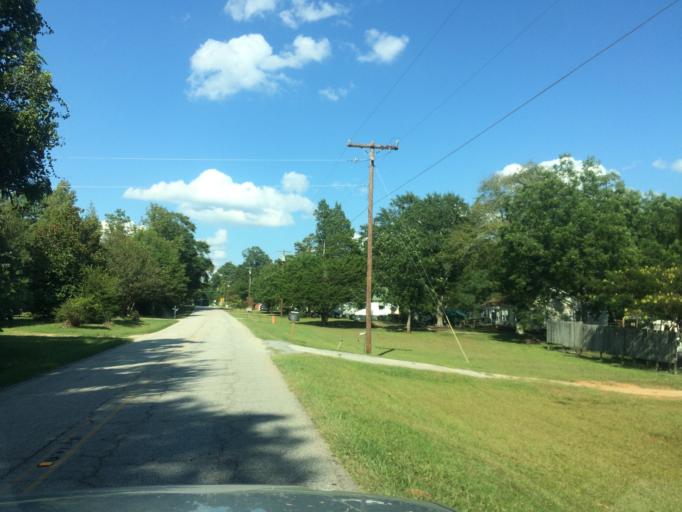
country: US
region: South Carolina
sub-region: Greenwood County
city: Ware Shoals
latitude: 34.4371
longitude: -82.2531
